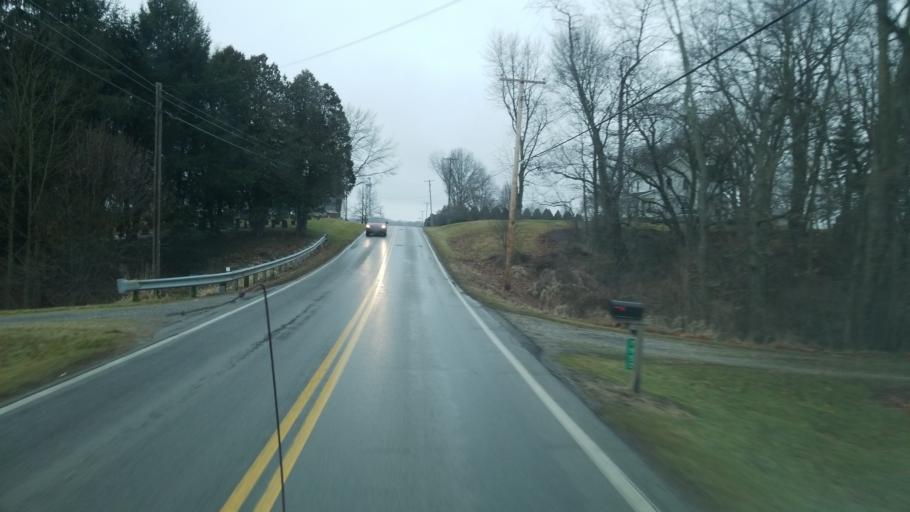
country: US
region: Ohio
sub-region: Wayne County
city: Smithville
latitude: 40.8590
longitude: -81.8297
